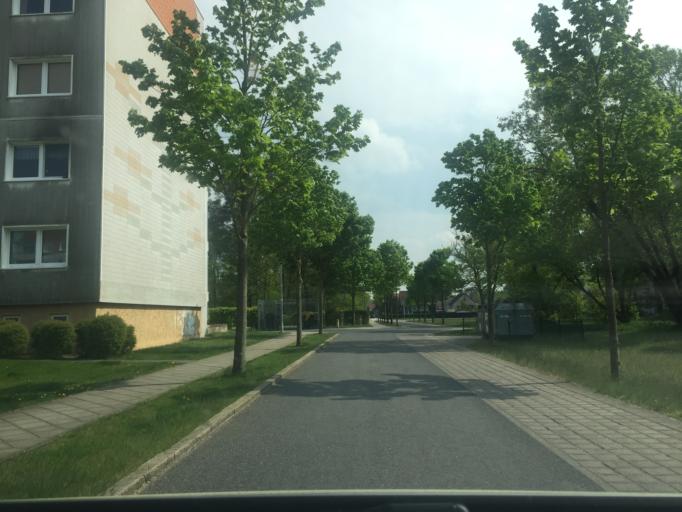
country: DE
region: Mecklenburg-Vorpommern
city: Torgelow
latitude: 53.6185
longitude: 14.0333
